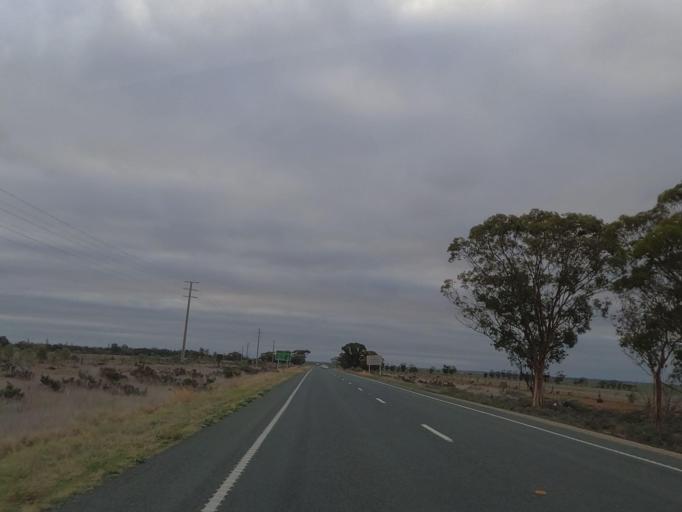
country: AU
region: Victoria
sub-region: Swan Hill
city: Swan Hill
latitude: -35.5681
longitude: 143.7849
